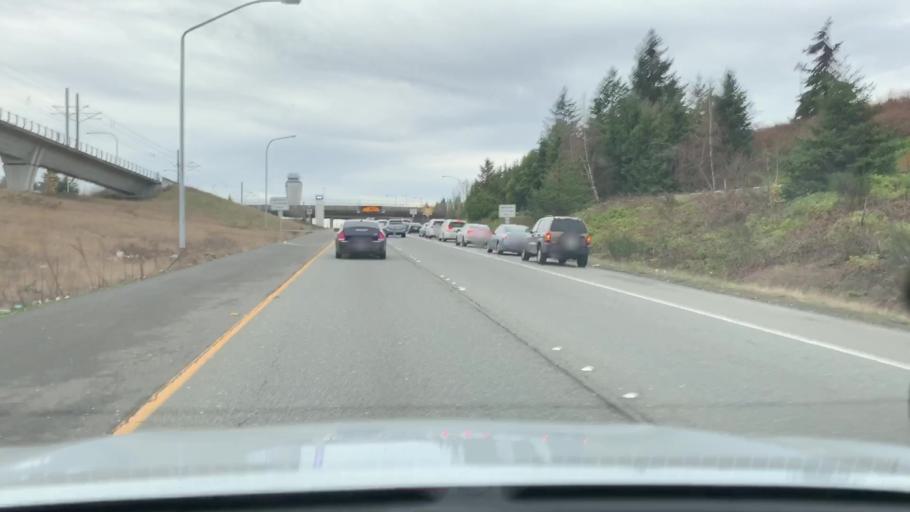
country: US
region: Washington
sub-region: King County
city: SeaTac
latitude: 47.4621
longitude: -122.2957
